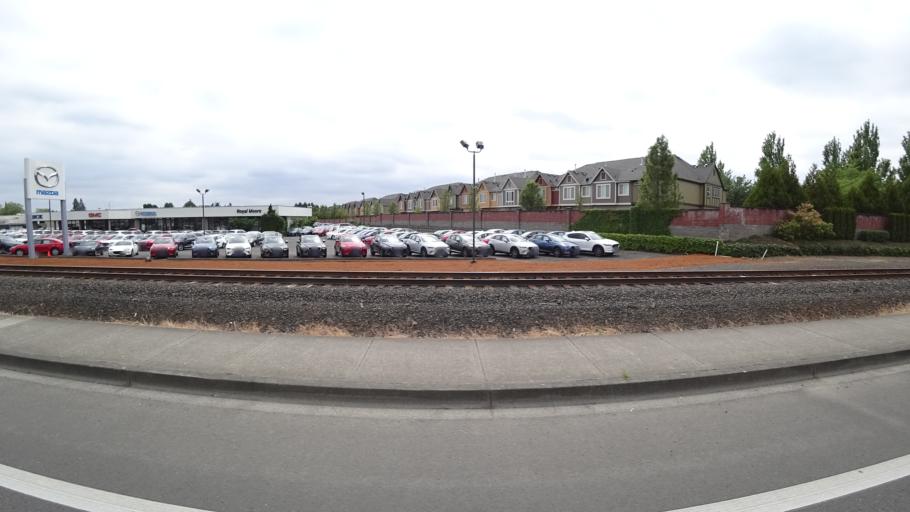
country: US
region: Oregon
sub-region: Washington County
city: Hillsboro
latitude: 45.5103
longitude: -122.9700
